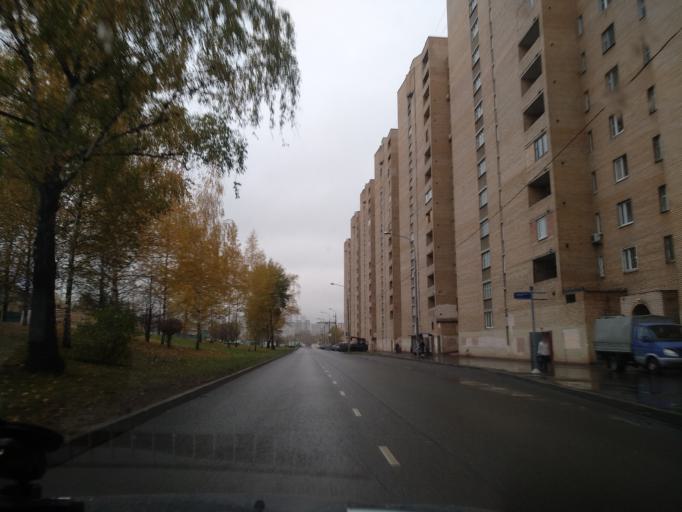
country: RU
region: Moscow
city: Otradnoye
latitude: 55.8739
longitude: 37.6053
